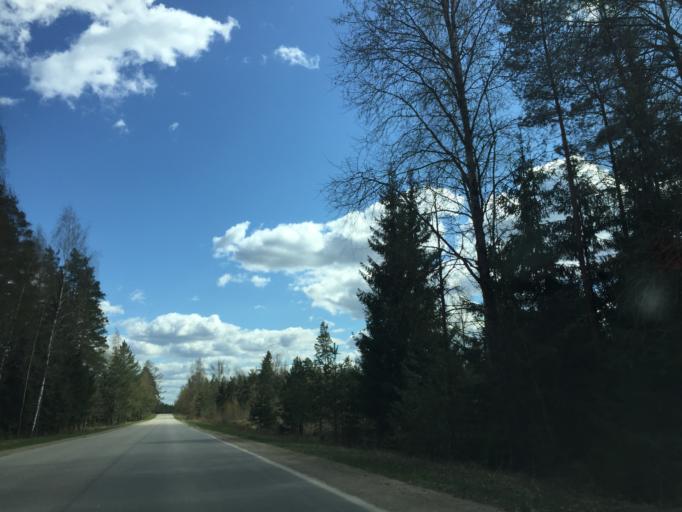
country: LV
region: Vilanu
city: Vilani
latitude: 56.5672
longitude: 27.0505
